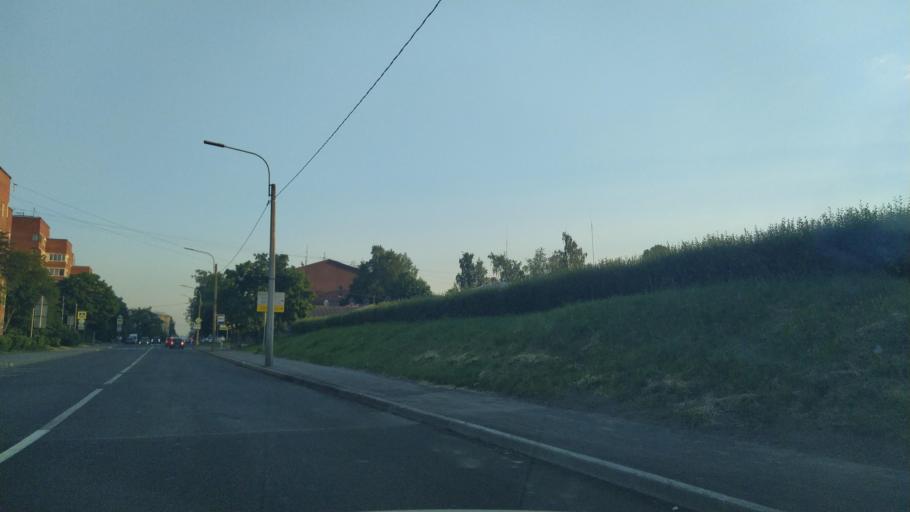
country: RU
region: St.-Petersburg
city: Kronshtadt
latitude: 60.0023
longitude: 29.7637
